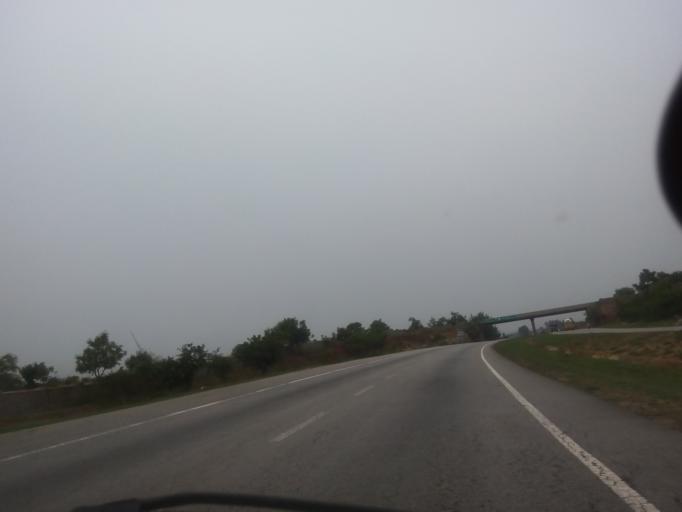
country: IN
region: Karnataka
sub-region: Bangalore Urban
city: Bangalore
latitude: 12.9129
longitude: 77.4673
